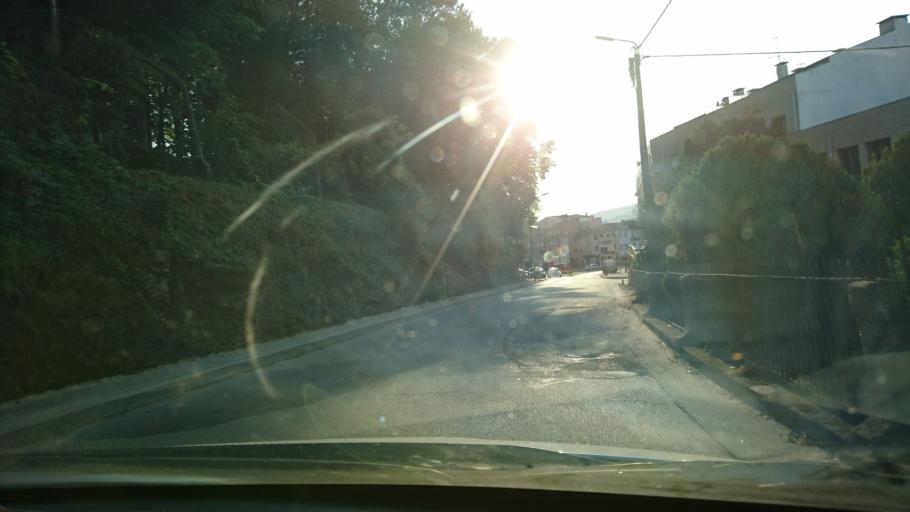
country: PT
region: Vila Real
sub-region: Mondim de Basto
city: Mondim de Basto
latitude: 41.4109
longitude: -7.9503
